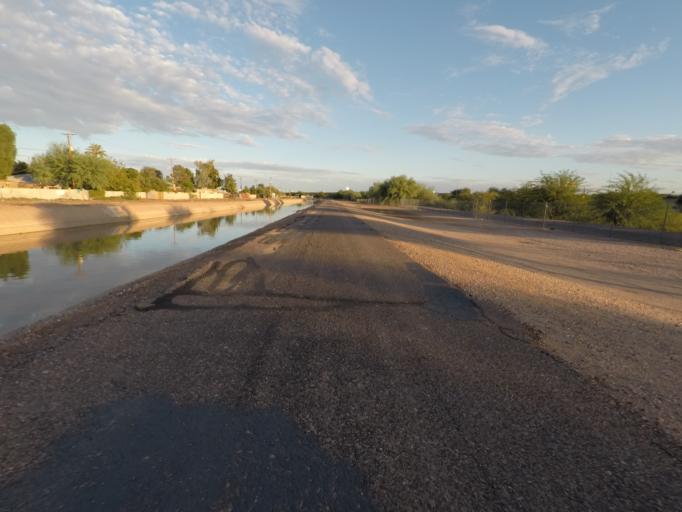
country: US
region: Arizona
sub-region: Maricopa County
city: Phoenix
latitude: 33.4625
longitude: -112.0118
